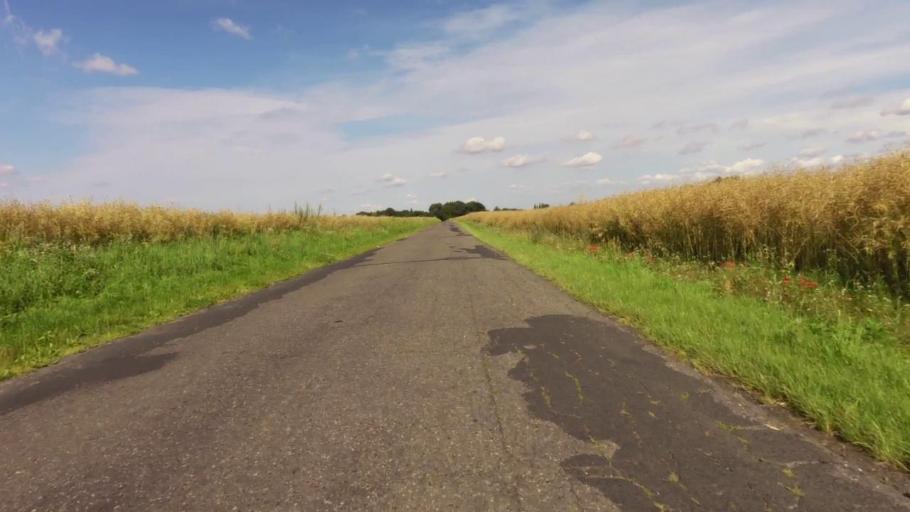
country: PL
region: West Pomeranian Voivodeship
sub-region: Powiat stargardzki
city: Stara Dabrowa
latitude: 53.3449
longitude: 15.1571
